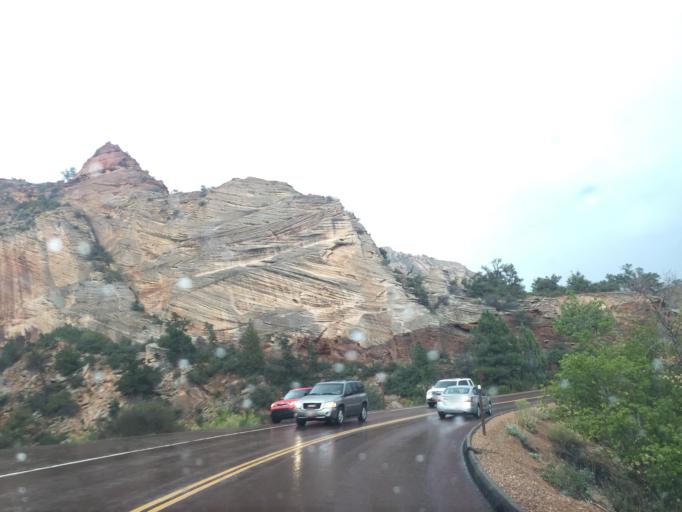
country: US
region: Utah
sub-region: Washington County
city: Hildale
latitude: 37.2146
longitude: -112.9396
